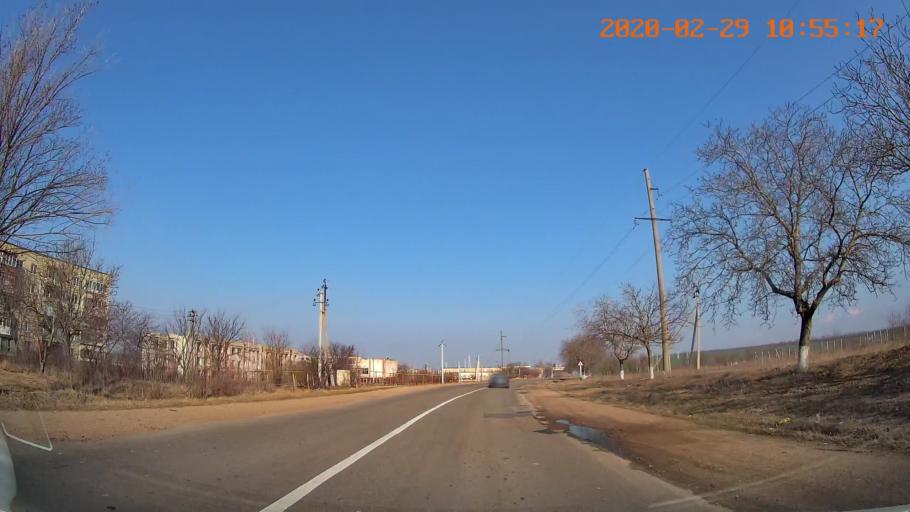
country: MD
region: Telenesti
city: Grigoriopol
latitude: 47.1322
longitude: 29.3250
